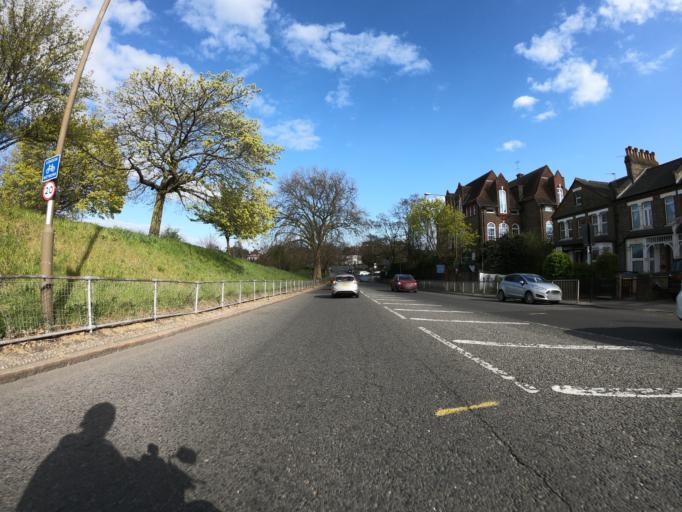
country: GB
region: England
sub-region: Greater London
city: Abbey Wood
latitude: 51.4800
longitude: 0.0857
